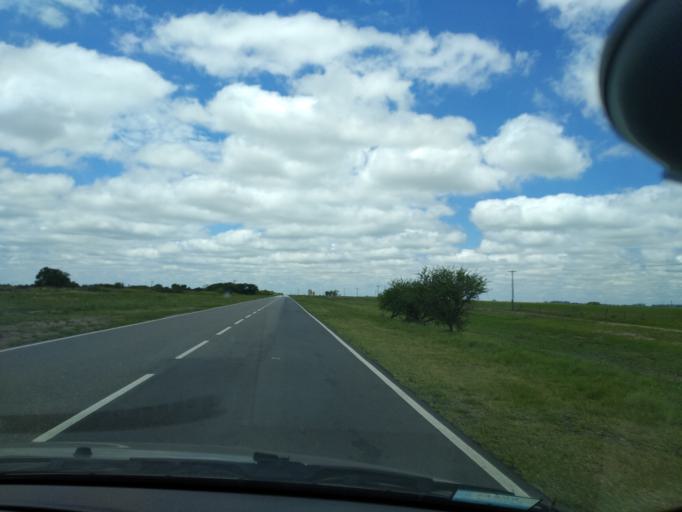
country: AR
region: Cordoba
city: Toledo
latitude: -31.6470
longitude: -64.0656
